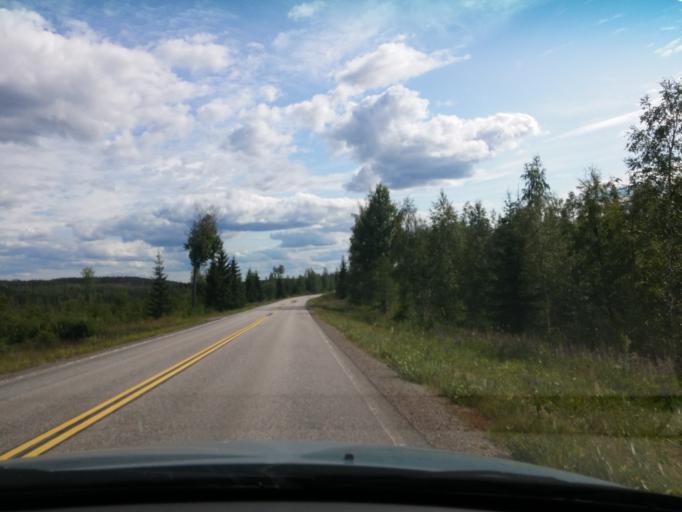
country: FI
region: Central Finland
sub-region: Keuruu
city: Keuruu
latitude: 62.3252
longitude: 24.7336
